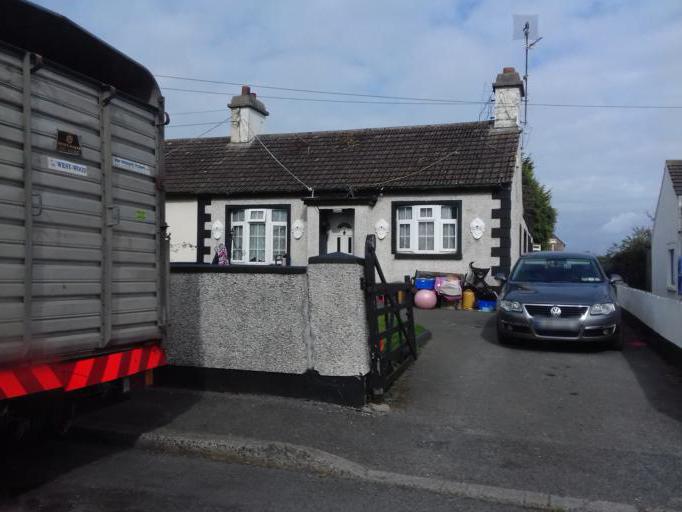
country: IE
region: Leinster
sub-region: Dublin City
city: Finglas
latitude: 53.4079
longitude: -6.2991
